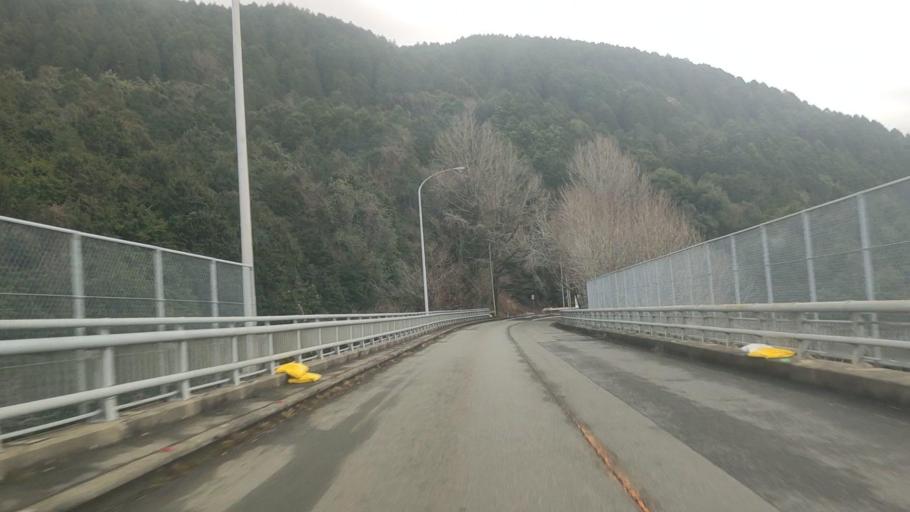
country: JP
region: Kumamoto
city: Hitoyoshi
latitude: 32.1211
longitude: 130.8135
